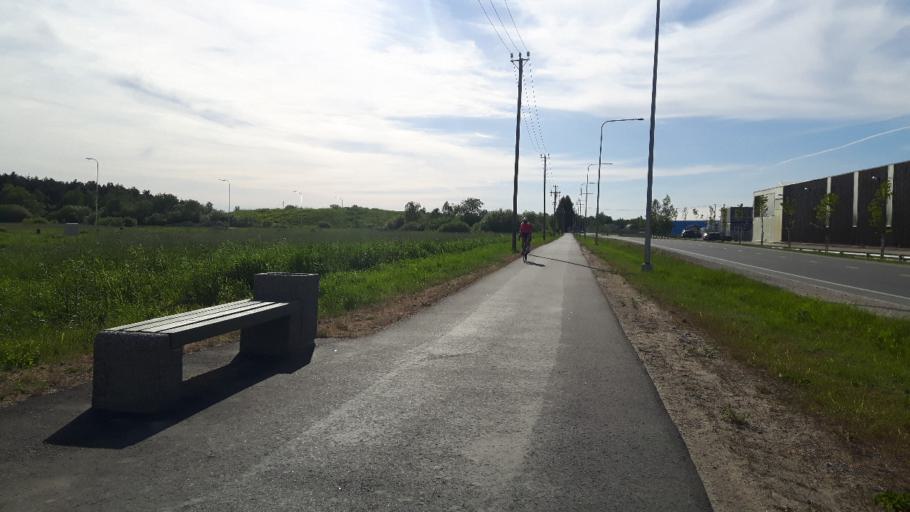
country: EE
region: Harju
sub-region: Joelaehtme vald
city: Loo
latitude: 59.4306
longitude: 24.9664
